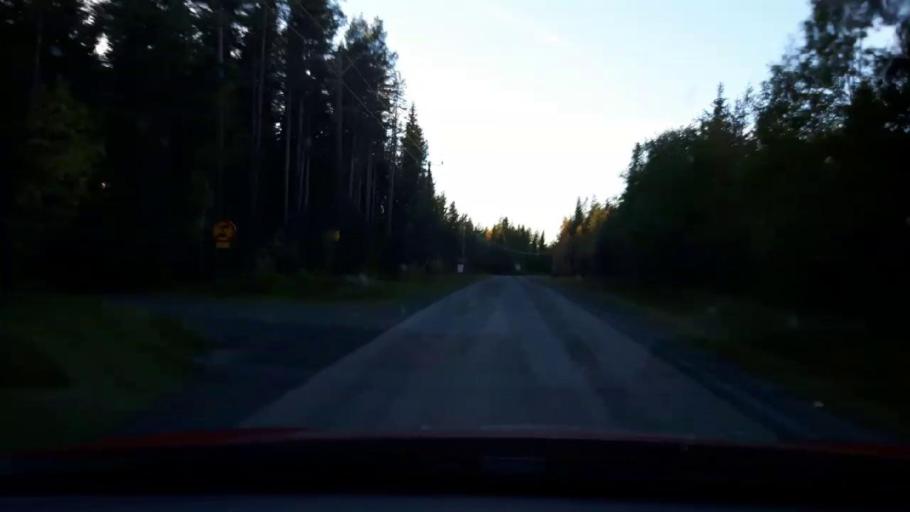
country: SE
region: Jaemtland
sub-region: Krokoms Kommun
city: Krokom
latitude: 63.4327
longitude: 14.4303
